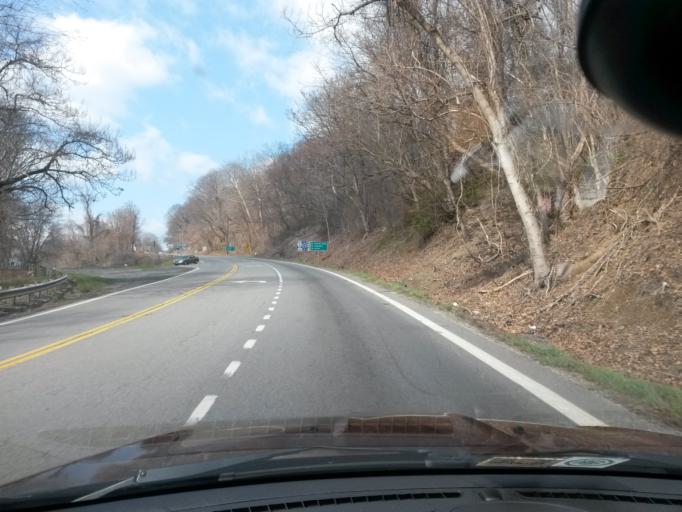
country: US
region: Virginia
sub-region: City of Waynesboro
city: Waynesboro
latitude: 38.0381
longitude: -78.8360
